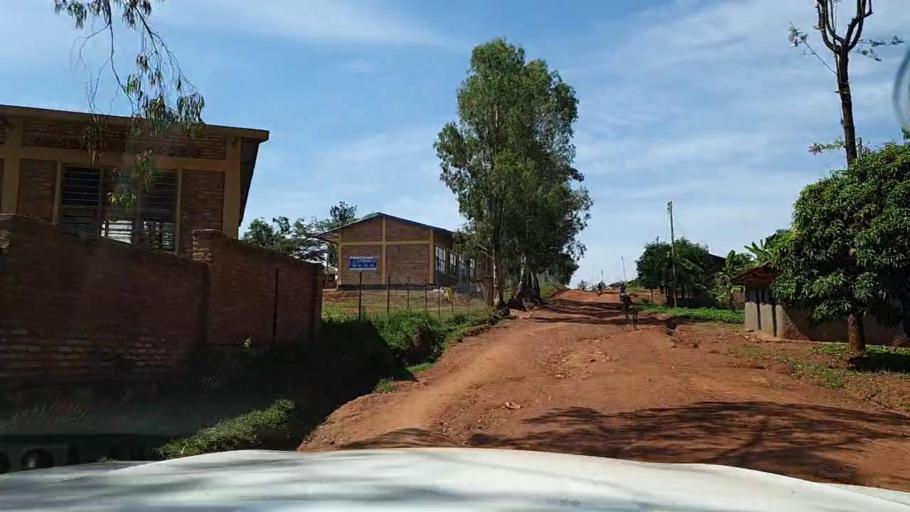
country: RW
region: Southern Province
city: Butare
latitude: -2.7173
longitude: 29.8391
